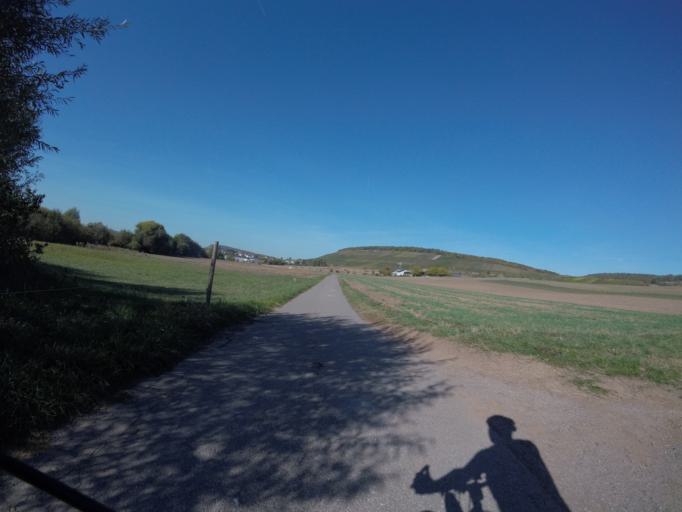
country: DE
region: Baden-Wuerttemberg
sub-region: Karlsruhe Region
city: Illingen
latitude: 48.9914
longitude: 8.9576
